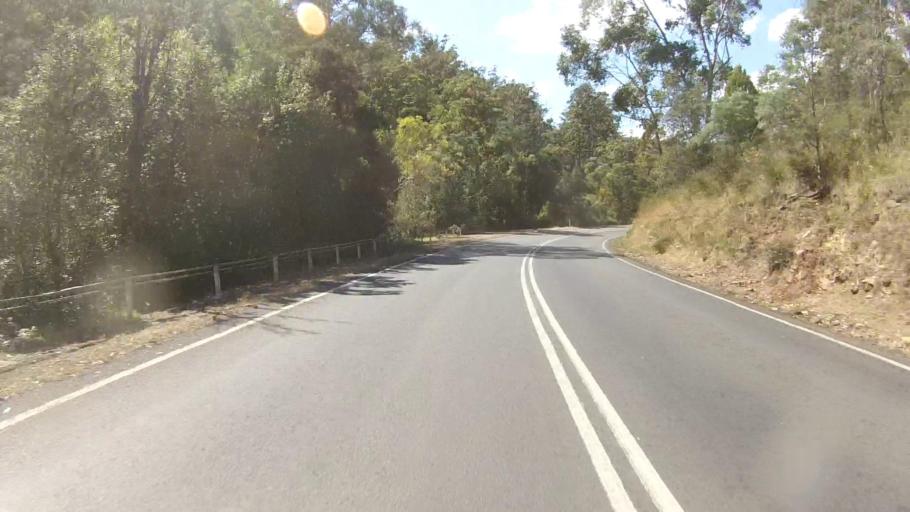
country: AU
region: Tasmania
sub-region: Derwent Valley
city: New Norfolk
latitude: -42.6769
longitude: 146.7576
